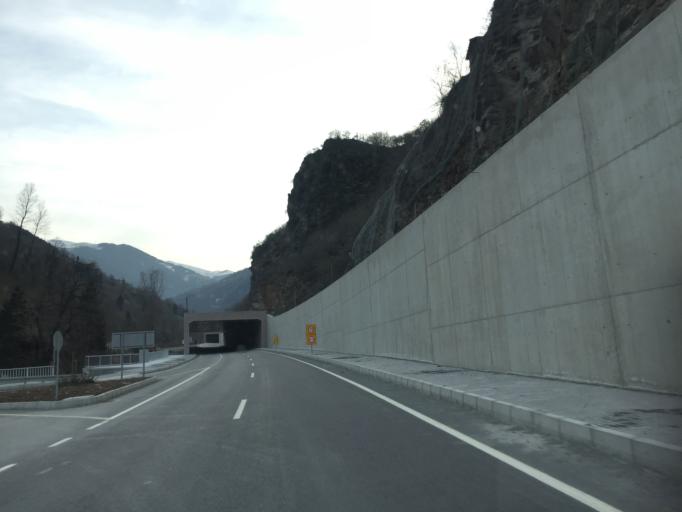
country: TR
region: Trabzon
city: Macka
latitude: 40.7783
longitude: 39.5690
